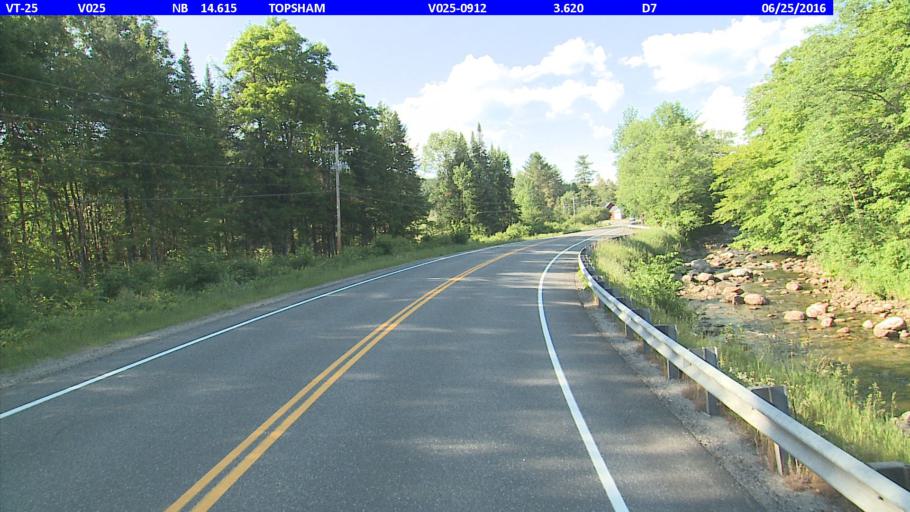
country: US
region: Vermont
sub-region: Orange County
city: Chelsea
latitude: 44.1027
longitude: -72.3196
